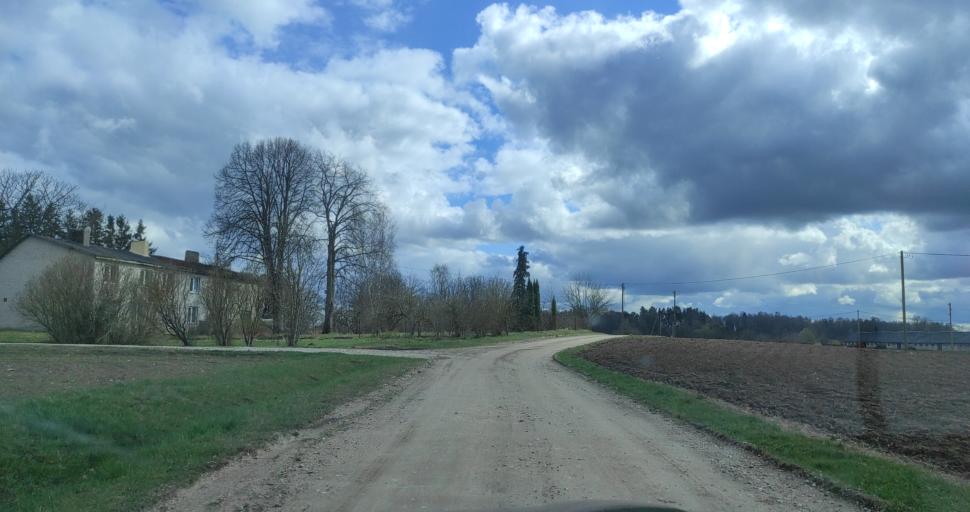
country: LV
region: Aizpute
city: Aizpute
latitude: 56.7131
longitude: 21.5851
